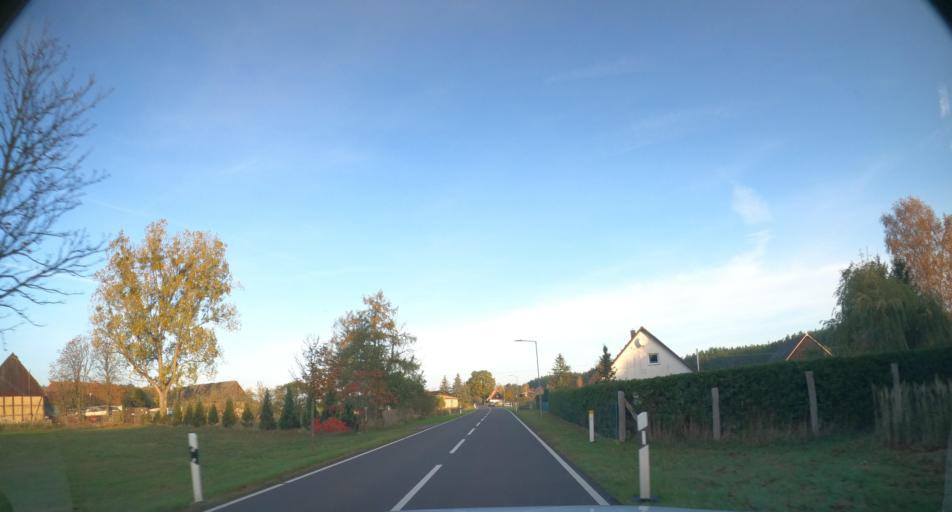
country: DE
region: Mecklenburg-Vorpommern
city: Ahlbeck
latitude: 53.6328
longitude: 14.2243
